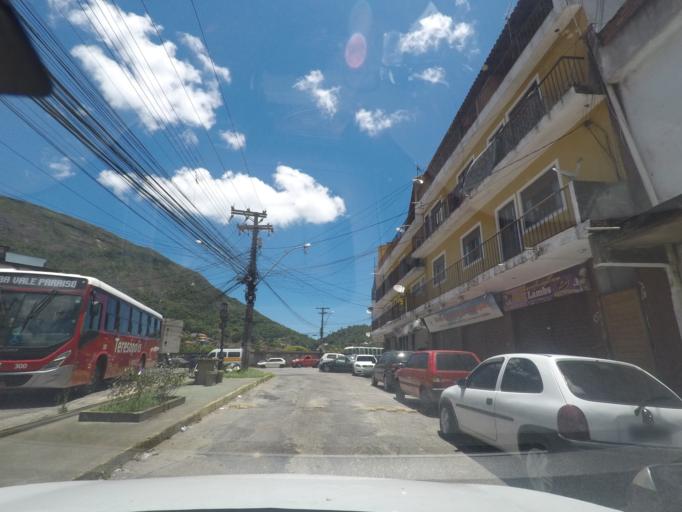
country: BR
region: Rio de Janeiro
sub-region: Teresopolis
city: Teresopolis
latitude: -22.4324
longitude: -42.9687
